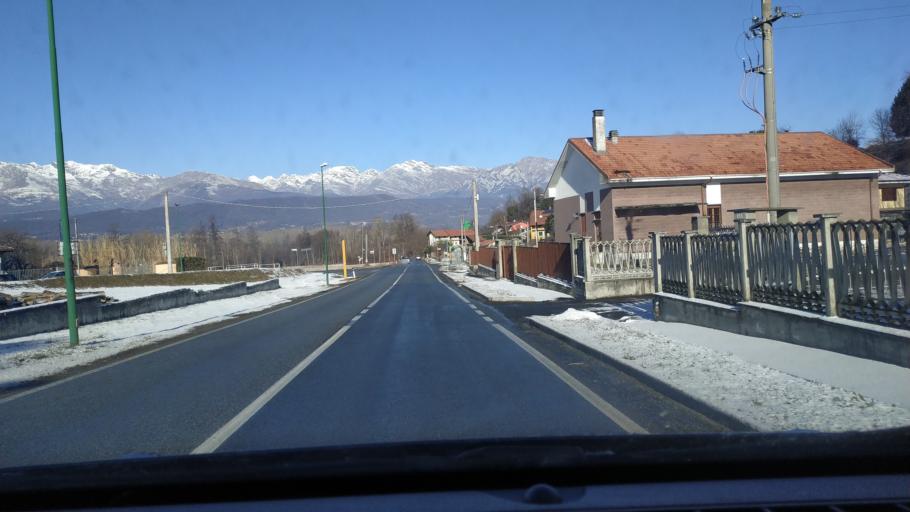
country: IT
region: Piedmont
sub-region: Provincia di Torino
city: Perosa Canavese
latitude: 45.3984
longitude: 7.8311
